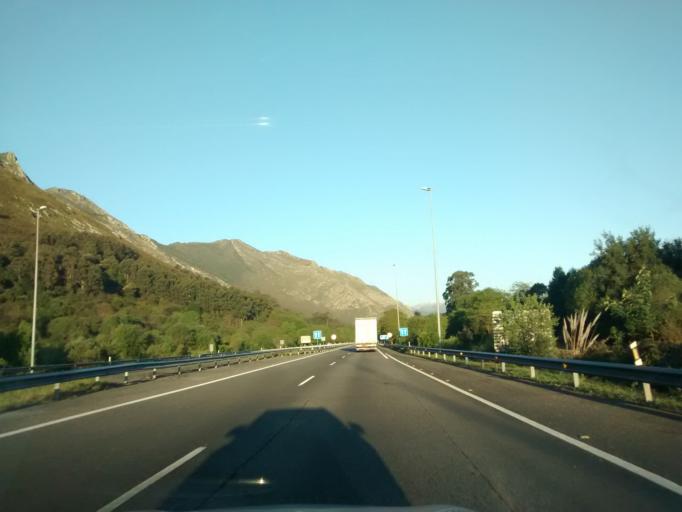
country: ES
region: Asturias
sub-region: Province of Asturias
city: Ribadesella
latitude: 43.4394
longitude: -4.9649
